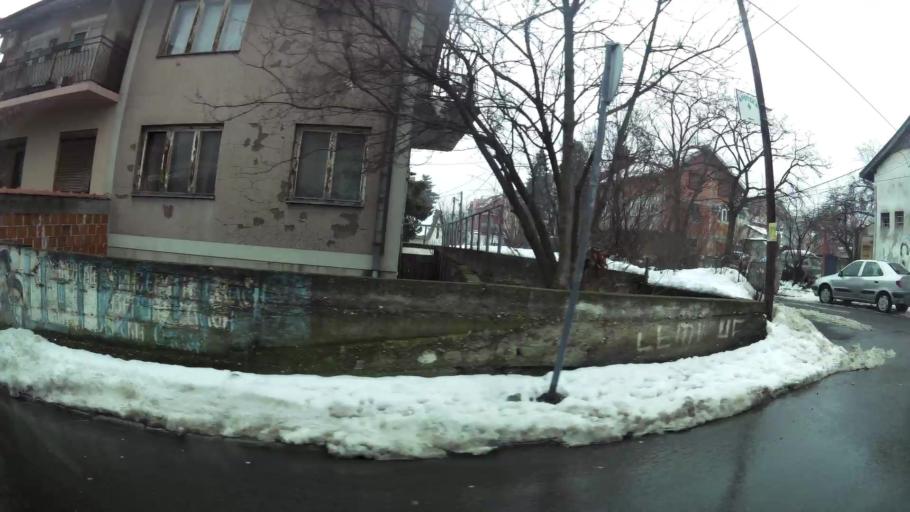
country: RS
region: Central Serbia
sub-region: Belgrade
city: Vozdovac
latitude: 44.7444
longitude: 20.5011
